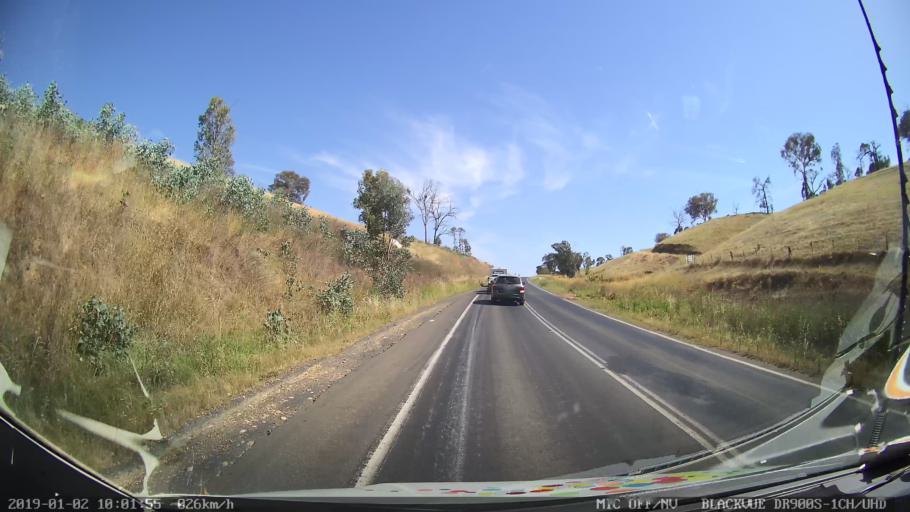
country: AU
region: New South Wales
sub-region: Gundagai
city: Gundagai
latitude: -35.1848
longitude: 148.1267
